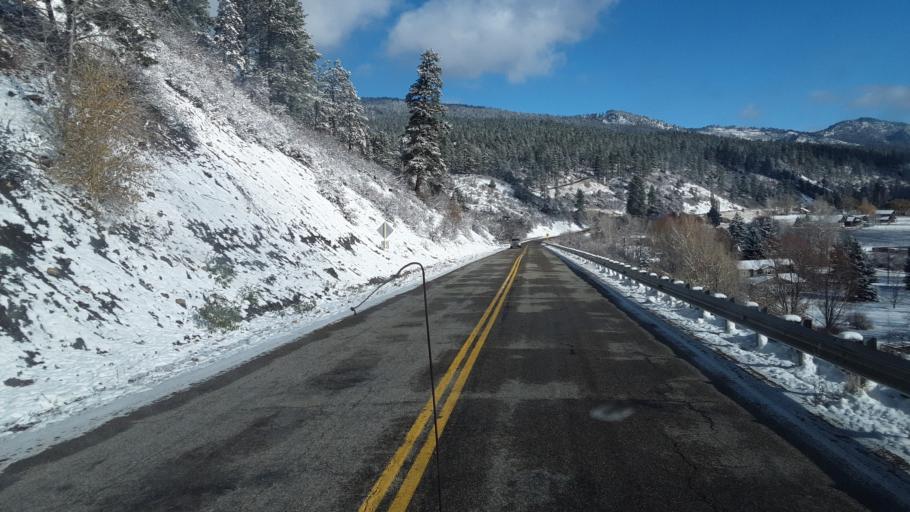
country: US
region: Colorado
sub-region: La Plata County
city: Durango
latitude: 37.3170
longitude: -107.7707
